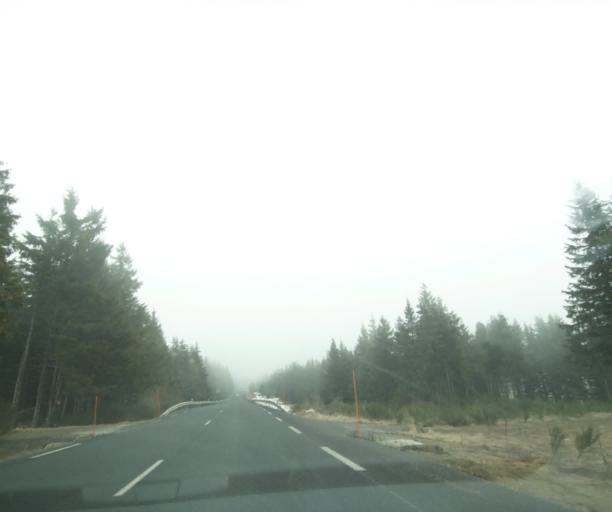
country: FR
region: Languedoc-Roussillon
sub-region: Departement de la Lozere
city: Langogne
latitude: 44.7529
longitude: 3.9423
